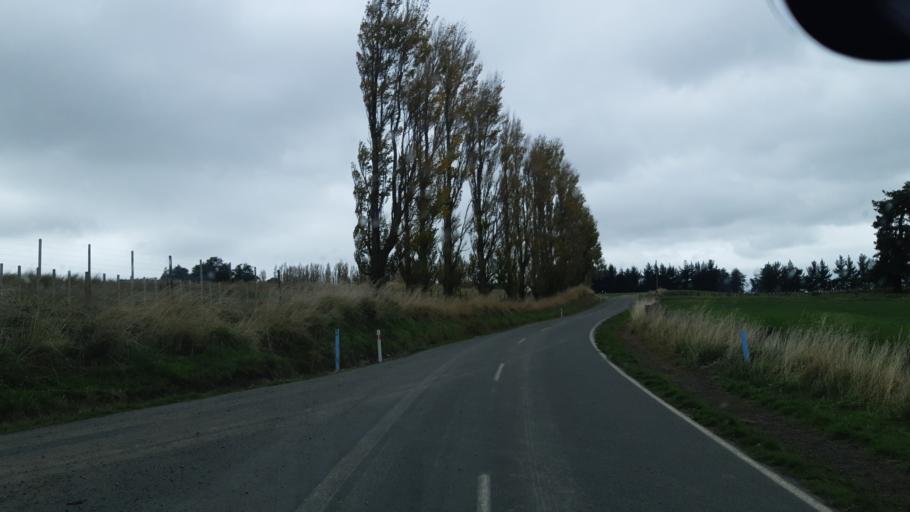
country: NZ
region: Manawatu-Wanganui
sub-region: Ruapehu District
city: Waiouru
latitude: -39.6184
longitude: 175.6339
